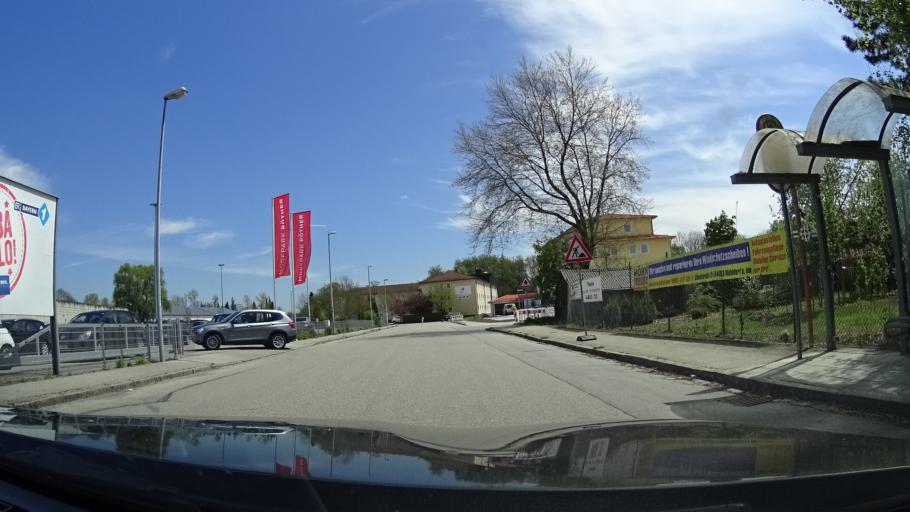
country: DE
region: Bavaria
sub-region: Upper Bavaria
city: Muehldorf
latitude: 48.2344
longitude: 12.5448
